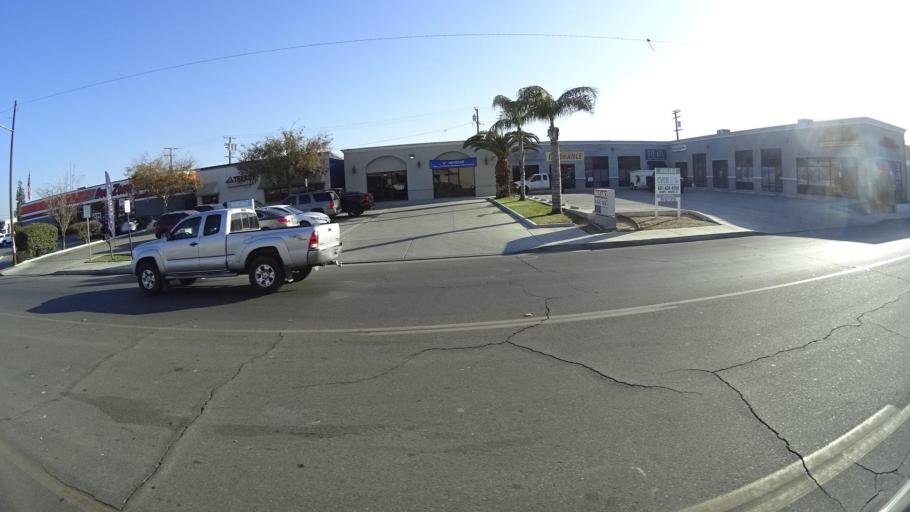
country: US
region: California
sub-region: Kern County
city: Delano
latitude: 35.7751
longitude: -119.2485
